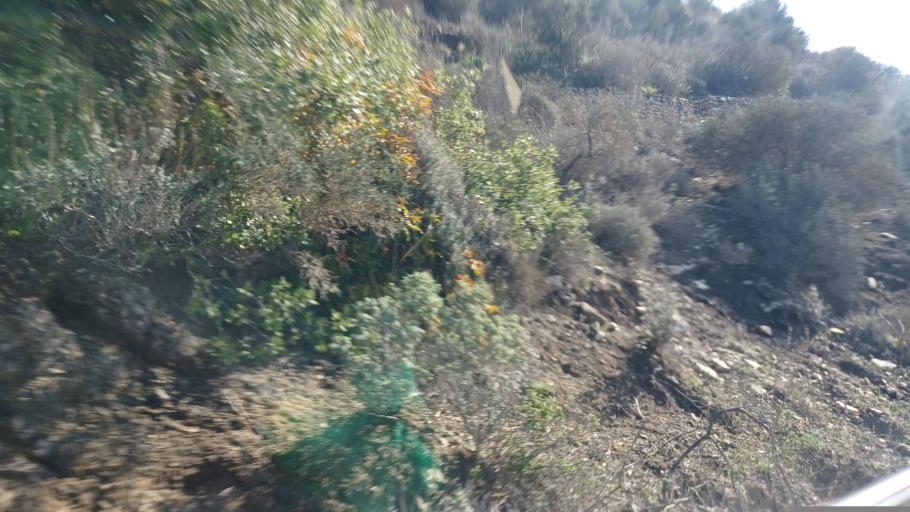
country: CY
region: Larnaka
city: Kofinou
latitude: 34.8458
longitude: 33.2954
